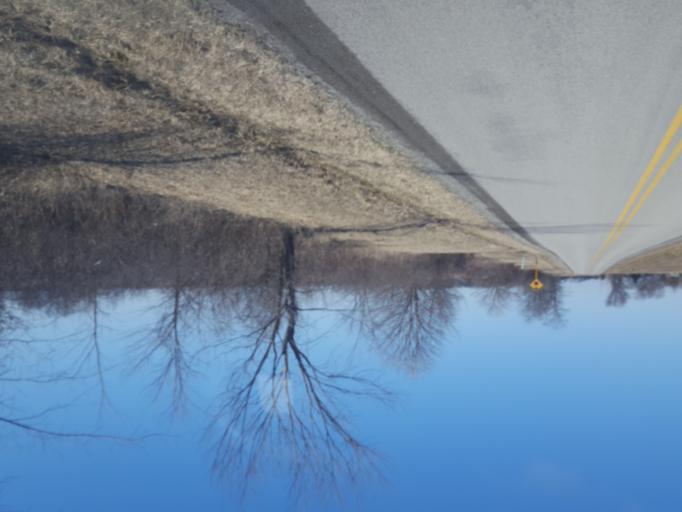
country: US
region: Ohio
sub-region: Wyandot County
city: Upper Sandusky
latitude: 40.7347
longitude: -83.2941
